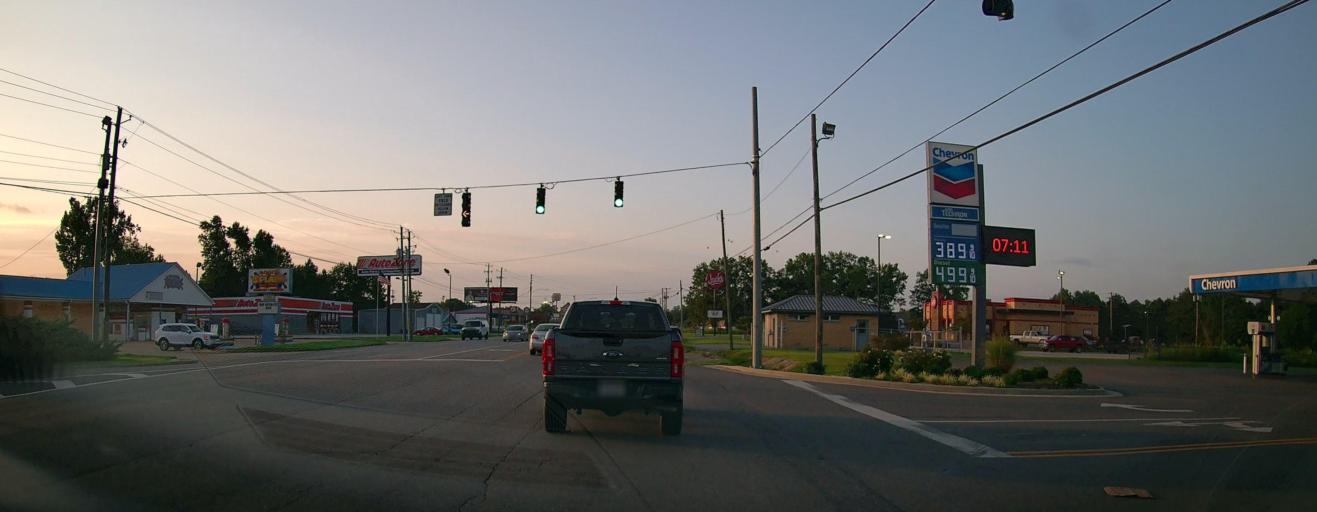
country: US
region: Alabama
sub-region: Marion County
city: Hamilton
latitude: 34.1192
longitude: -87.9895
